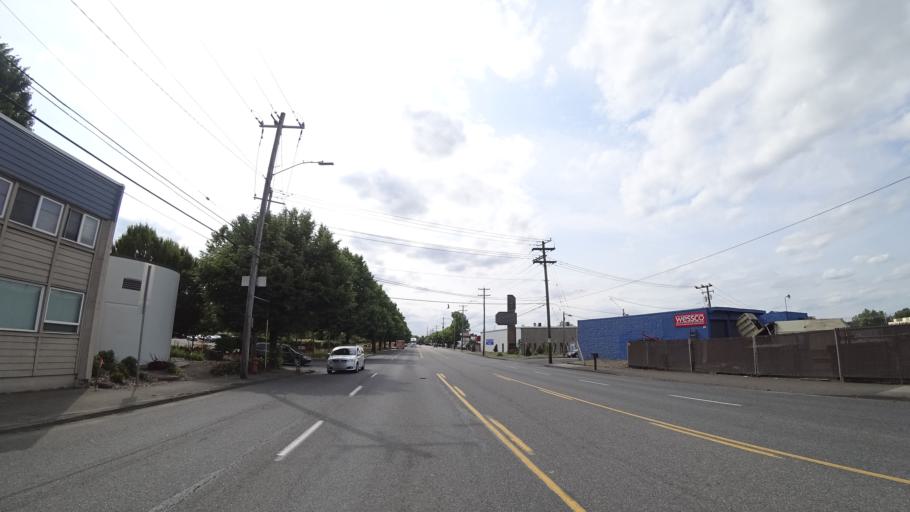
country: US
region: Washington
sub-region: Clark County
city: Vancouver
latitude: 45.5816
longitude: -122.6629
